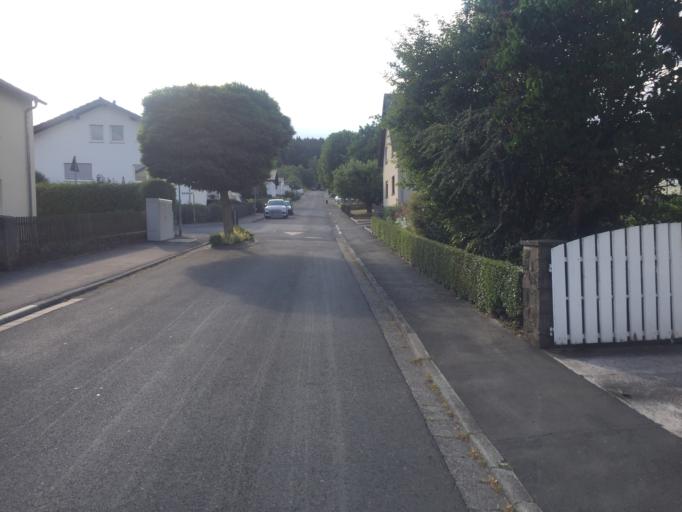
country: DE
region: Hesse
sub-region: Regierungsbezirk Giessen
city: Heuchelheim
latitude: 50.6409
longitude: 8.5965
